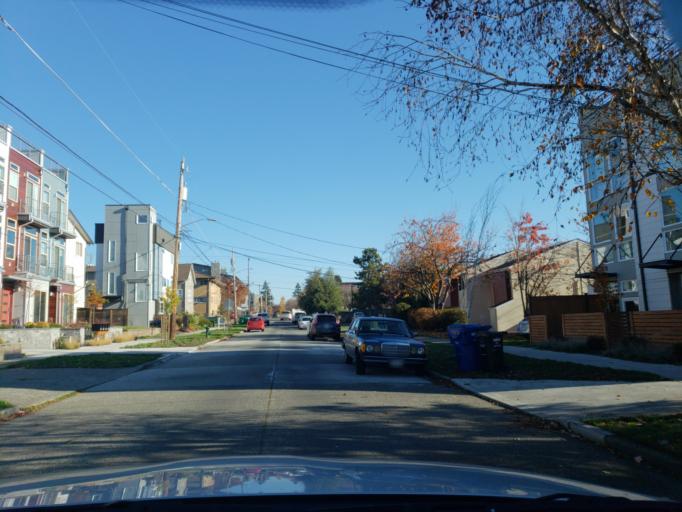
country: US
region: Washington
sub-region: King County
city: Seattle
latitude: 47.6738
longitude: -122.3893
